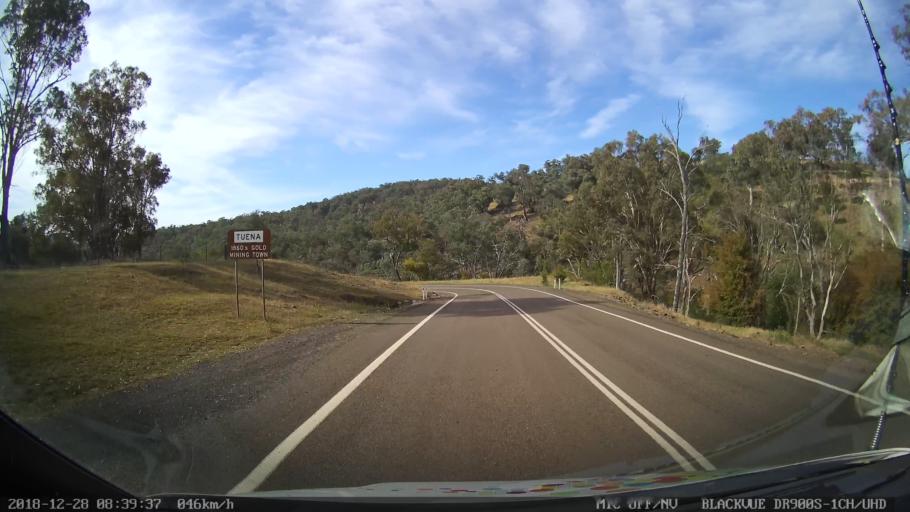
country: AU
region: New South Wales
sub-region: Upper Lachlan Shire
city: Crookwell
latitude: -34.0134
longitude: 149.3184
